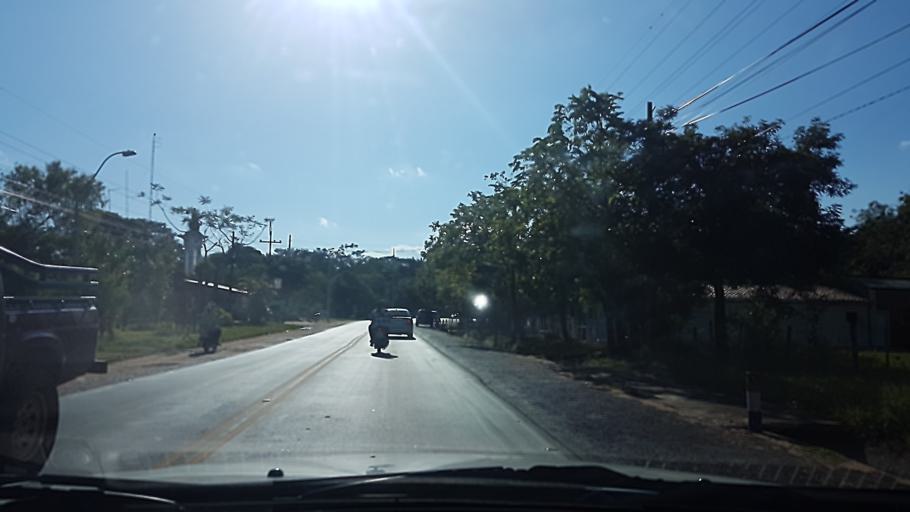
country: PY
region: Central
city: San Antonio
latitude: -25.4445
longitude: -57.5329
